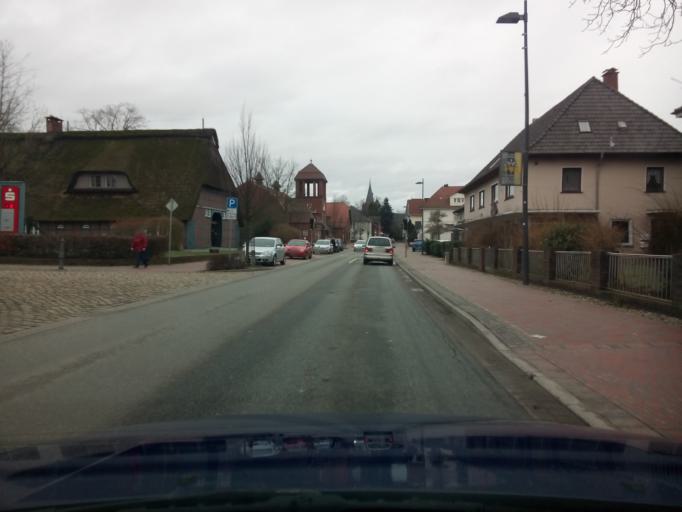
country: DE
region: Lower Saxony
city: Ritterhude
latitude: 53.1791
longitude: 8.7516
